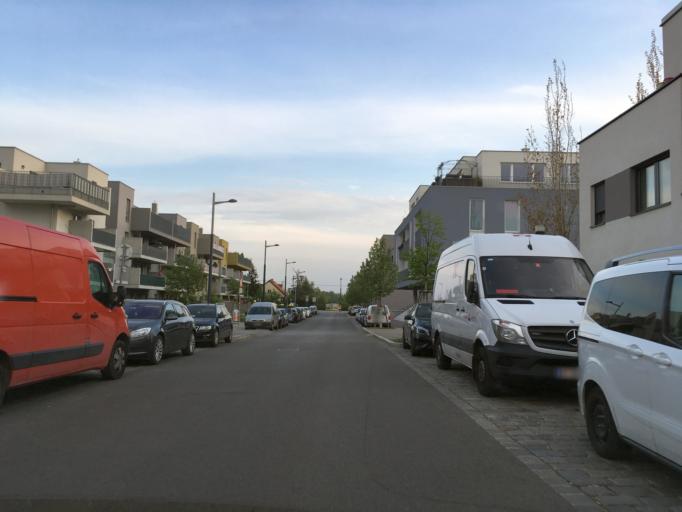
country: AT
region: Lower Austria
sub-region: Politischer Bezirk Wien-Umgebung
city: Gerasdorf bei Wien
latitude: 48.2873
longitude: 16.4349
